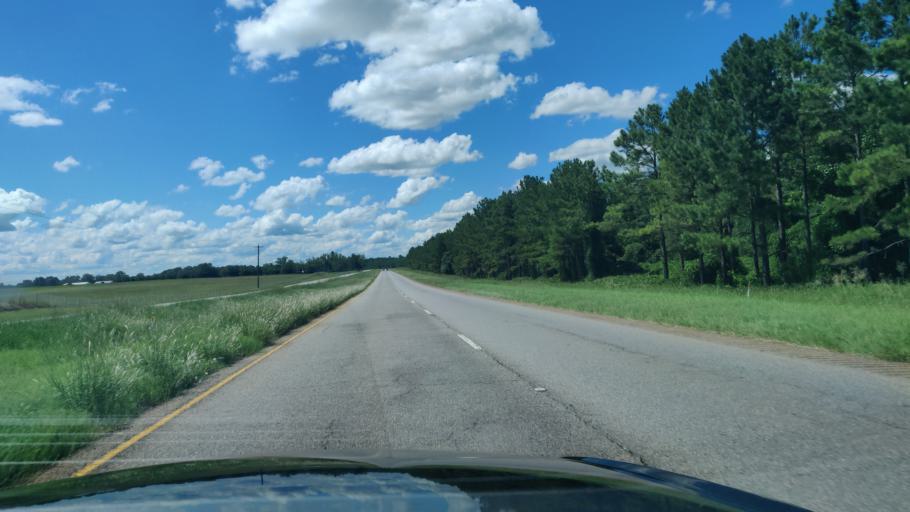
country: US
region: Georgia
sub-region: Stewart County
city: Richland
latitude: 32.0143
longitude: -84.6591
